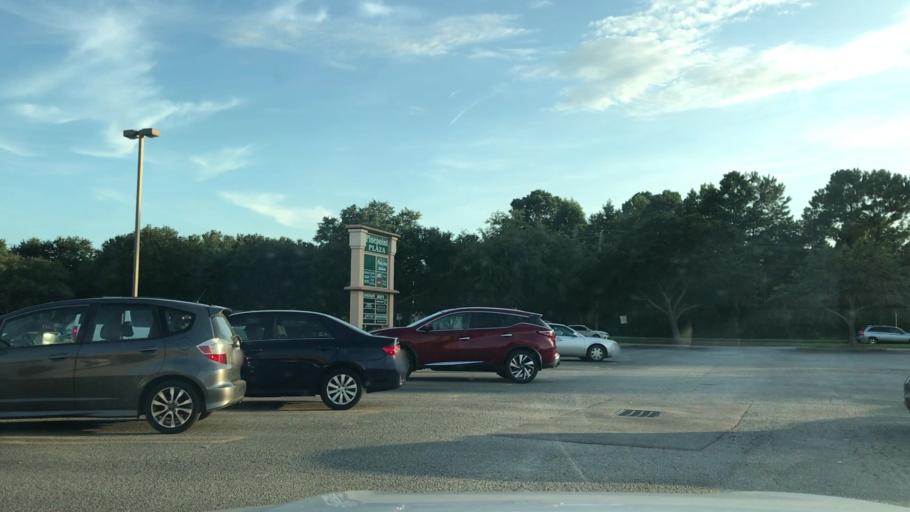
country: US
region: South Carolina
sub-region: Charleston County
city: North Charleston
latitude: 32.8087
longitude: -80.0237
